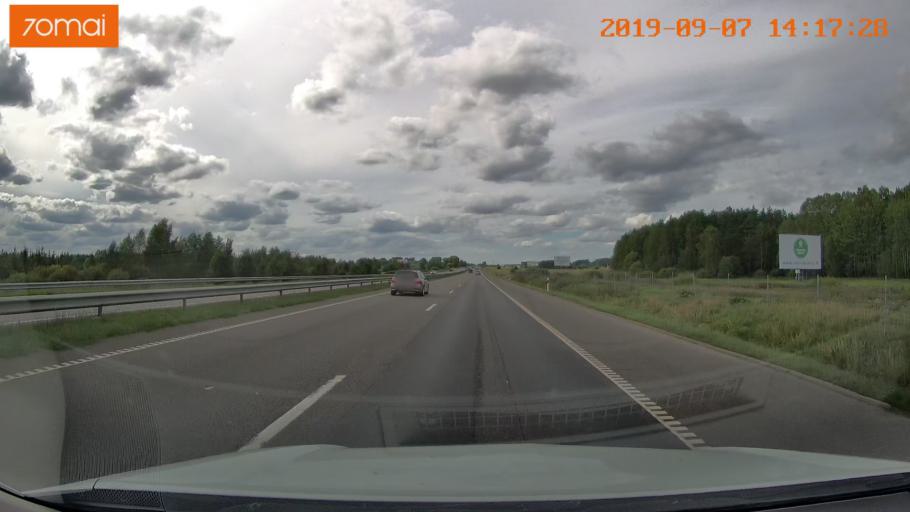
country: LT
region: Vilnius County
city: Elektrenai
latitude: 54.7956
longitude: 24.5854
